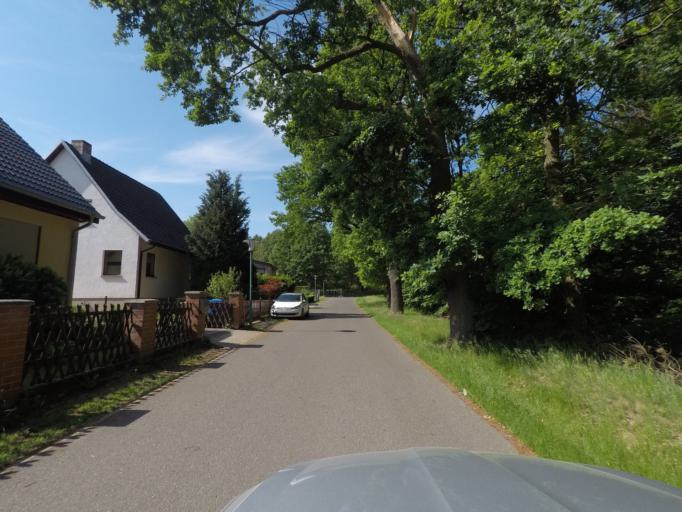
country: DE
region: Brandenburg
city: Melchow
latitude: 52.8645
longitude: 13.7153
